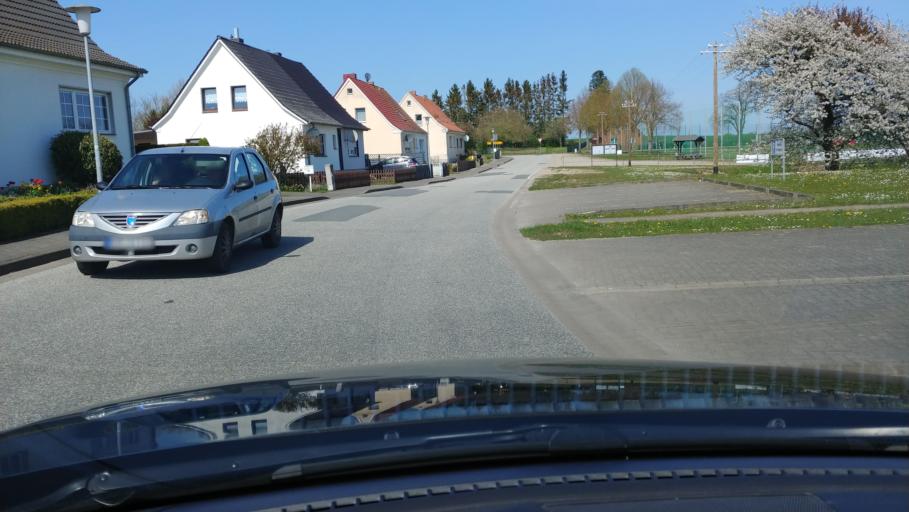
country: DE
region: Mecklenburg-Vorpommern
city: Muhlen Eichsen
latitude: 53.8020
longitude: 11.2664
